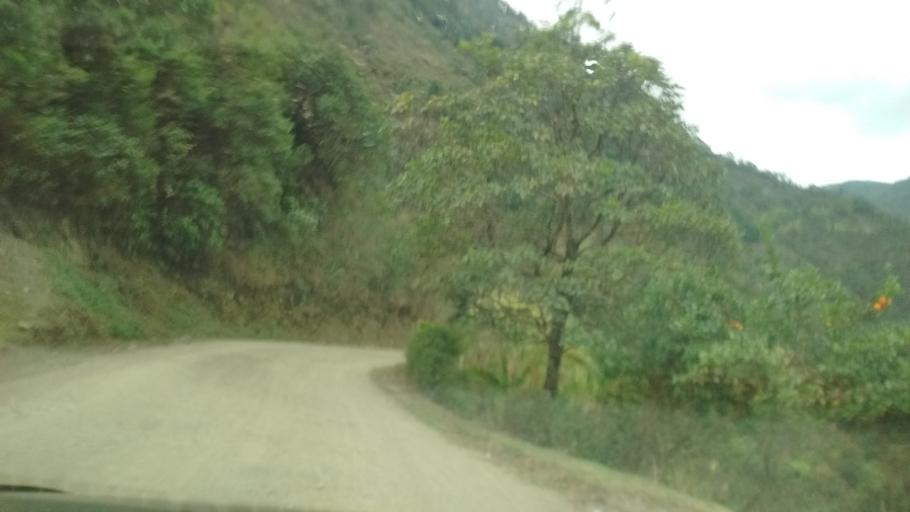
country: CO
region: Cauca
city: La Vega
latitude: 2.0445
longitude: -76.8013
